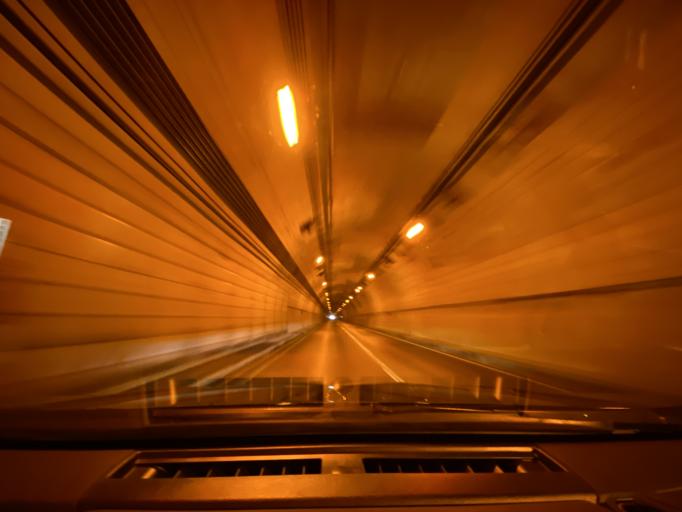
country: JP
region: Hokkaido
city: Rumoi
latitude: 43.7955
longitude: 141.3760
